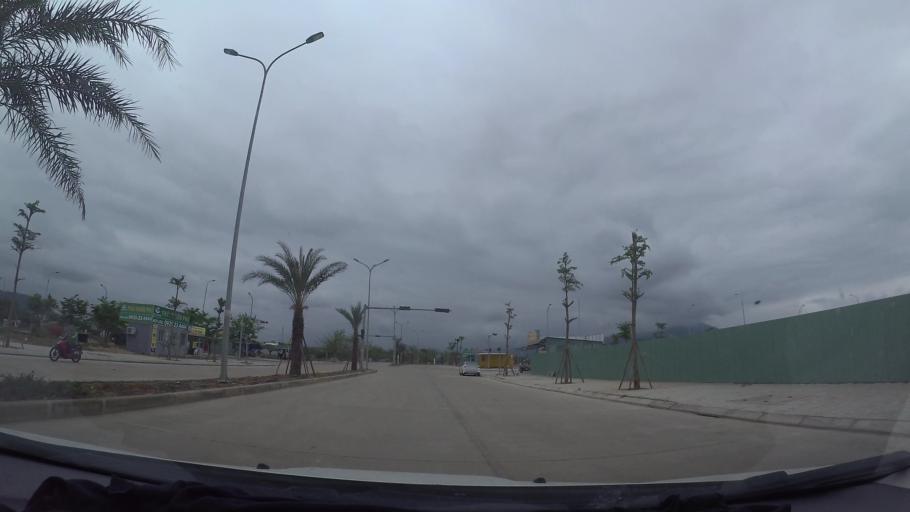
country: VN
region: Da Nang
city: Lien Chieu
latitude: 16.1061
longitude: 108.1182
